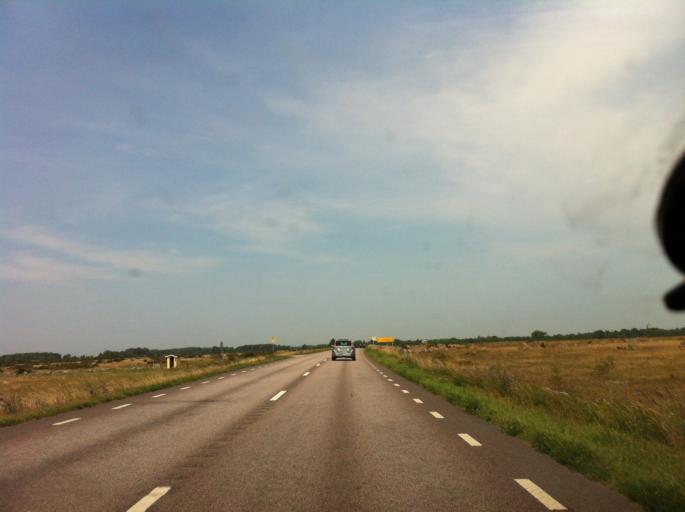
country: SE
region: Kalmar
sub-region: Borgholms Kommun
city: Borgholm
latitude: 56.9772
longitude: 16.8065
